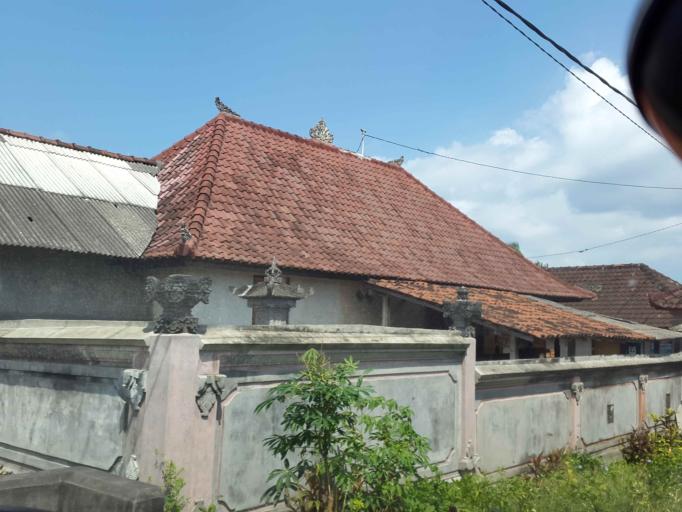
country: ID
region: Bali
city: Klungkung
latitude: -8.5583
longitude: 115.3813
